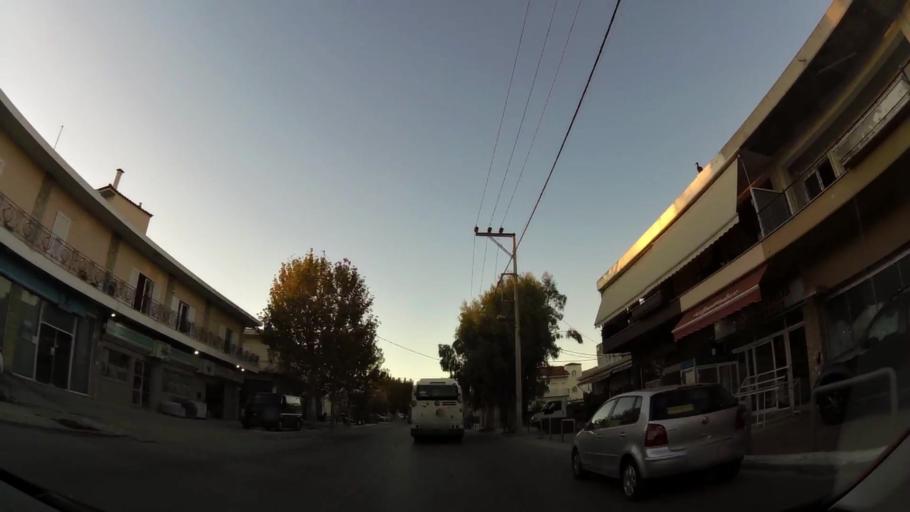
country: GR
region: Attica
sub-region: Nomarchia Dytikis Attikis
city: Ano Liosia
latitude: 38.0798
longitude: 23.6991
